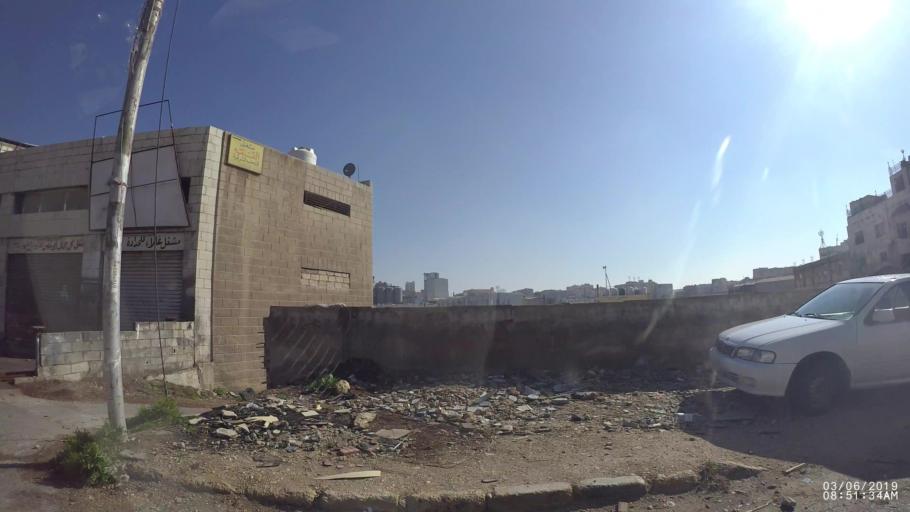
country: JO
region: Amman
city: Amman
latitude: 31.9865
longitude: 35.9921
